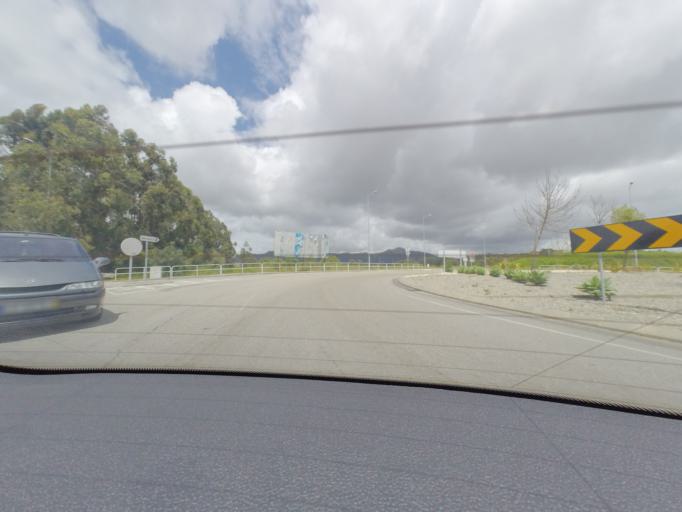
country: PT
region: Lisbon
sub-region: Cascais
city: Alcabideche
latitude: 38.7409
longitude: -9.3974
